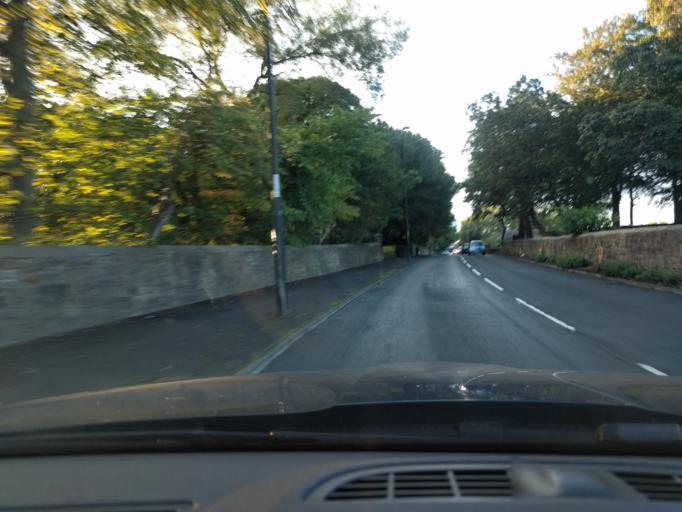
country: GB
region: England
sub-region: Northumberland
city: Backworth
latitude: 55.0385
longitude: -1.5265
